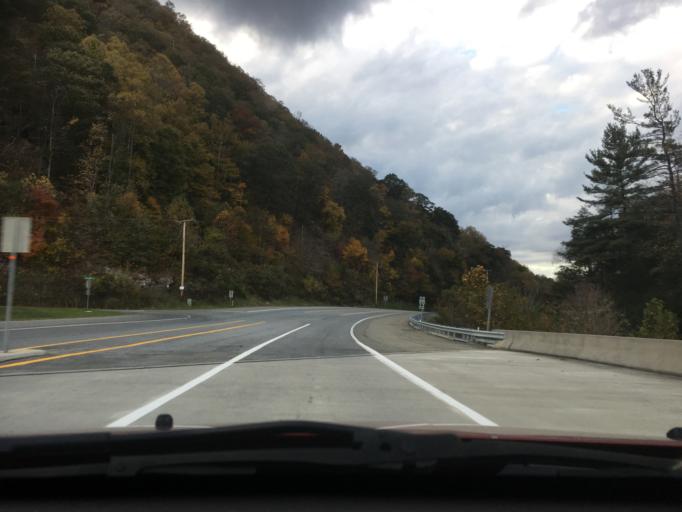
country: US
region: Virginia
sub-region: Pulaski County
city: Dublin
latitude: 37.1970
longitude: -80.7333
